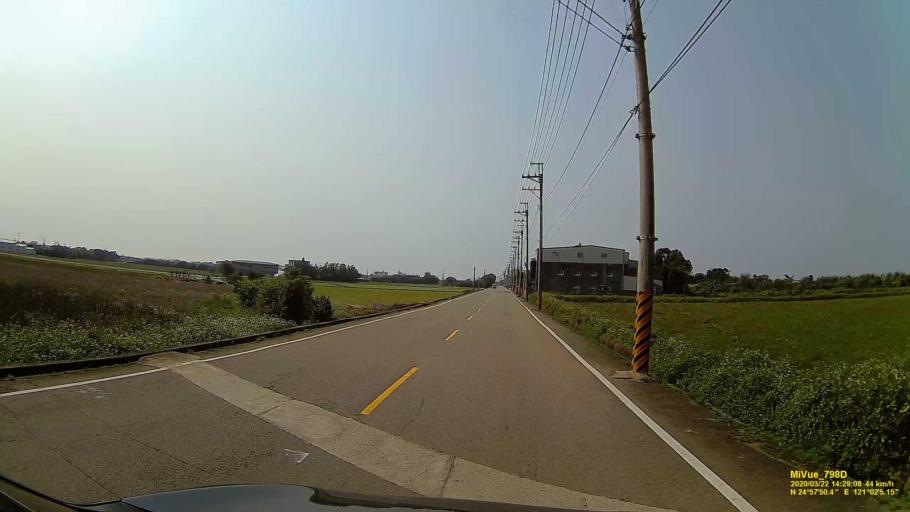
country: TW
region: Taiwan
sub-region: Hsinchu
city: Zhubei
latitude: 24.9642
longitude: 121.0343
